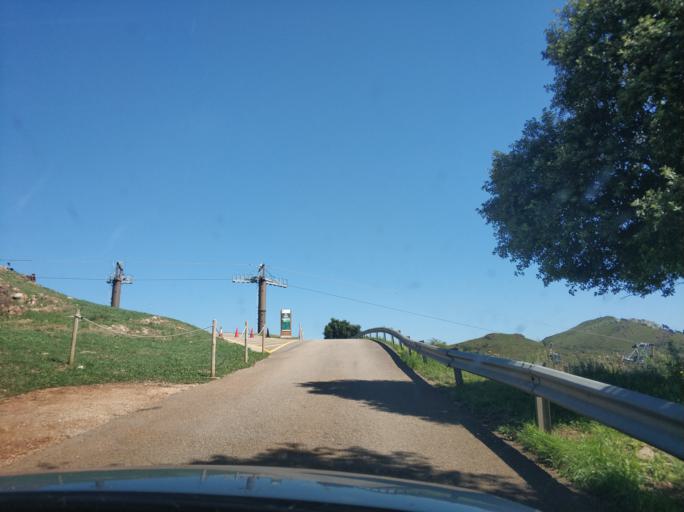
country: ES
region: Cantabria
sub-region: Provincia de Cantabria
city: Penagos
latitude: 43.3666
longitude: -3.8364
